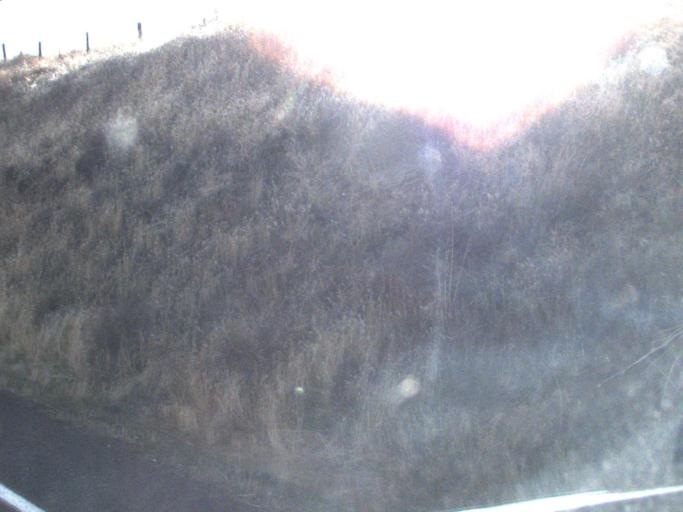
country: US
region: Washington
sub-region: Columbia County
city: Dayton
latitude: 46.4779
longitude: -117.9606
